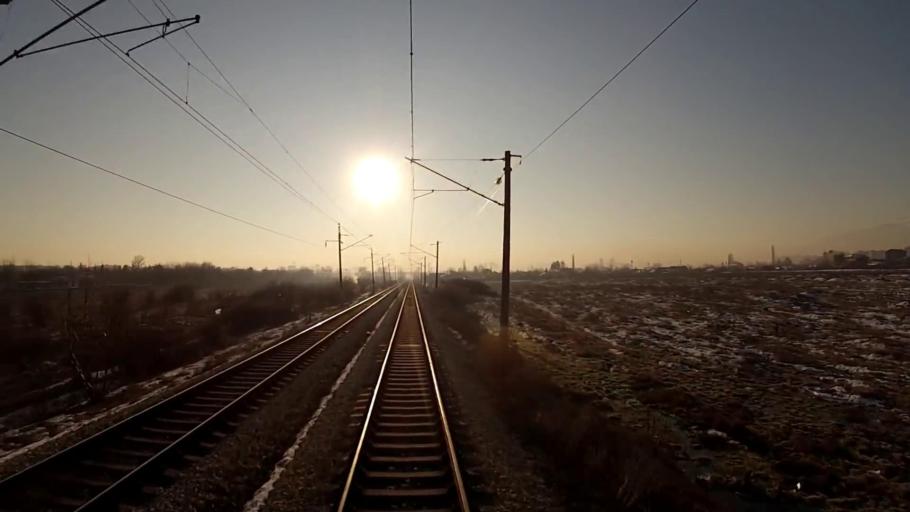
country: BG
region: Sofiya
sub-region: Obshtina Bozhurishte
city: Bozhurishte
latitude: 42.7404
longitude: 23.2618
